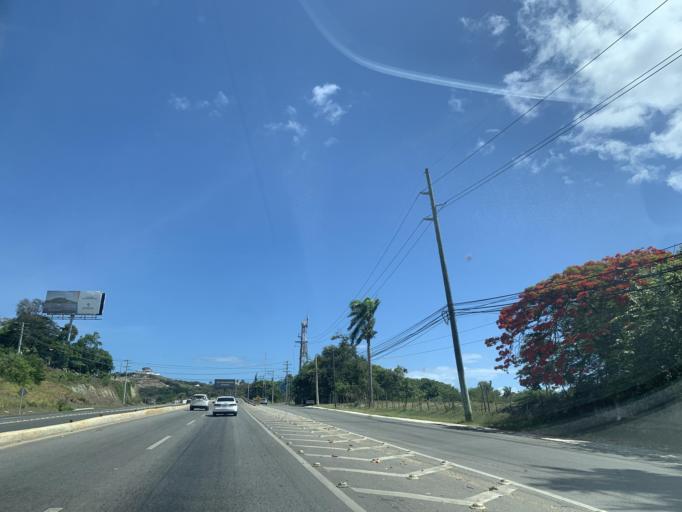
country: DO
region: Puerto Plata
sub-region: Puerto Plata
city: Puerto Plata
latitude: 19.8142
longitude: -70.7317
